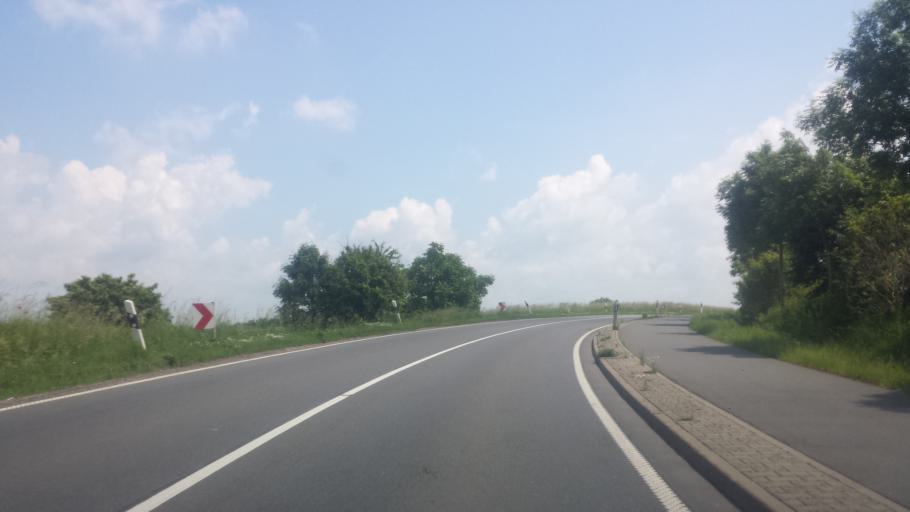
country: DE
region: Hesse
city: Reinheim
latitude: 49.8500
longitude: 8.8079
